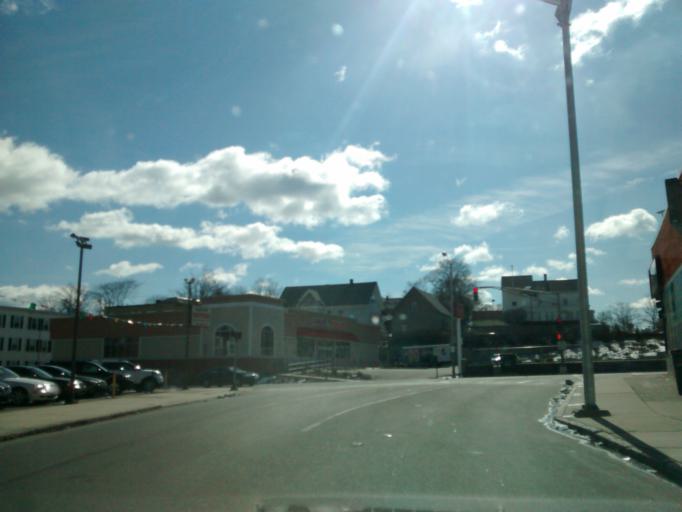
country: US
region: Massachusetts
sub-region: Worcester County
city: Worcester
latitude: 42.2548
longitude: -71.8148
